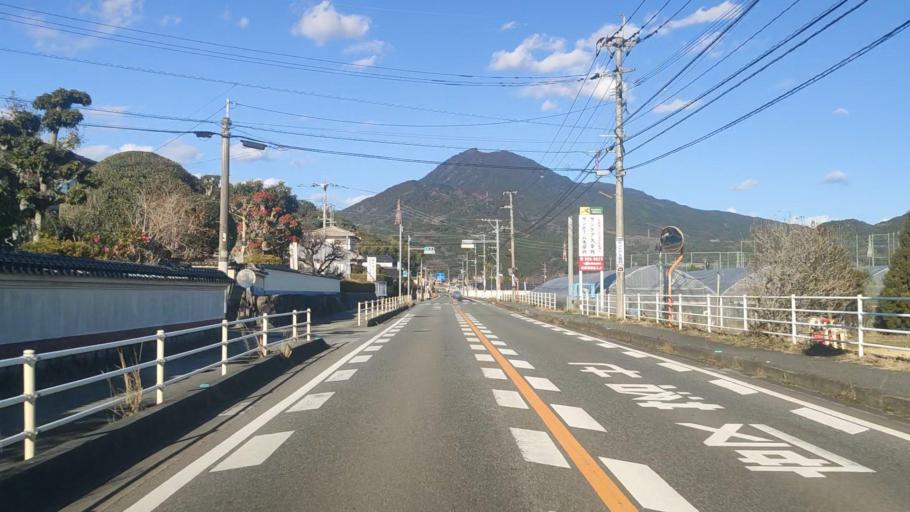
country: JP
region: Fukuoka
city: Dazaifu
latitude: 33.5013
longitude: 130.5497
